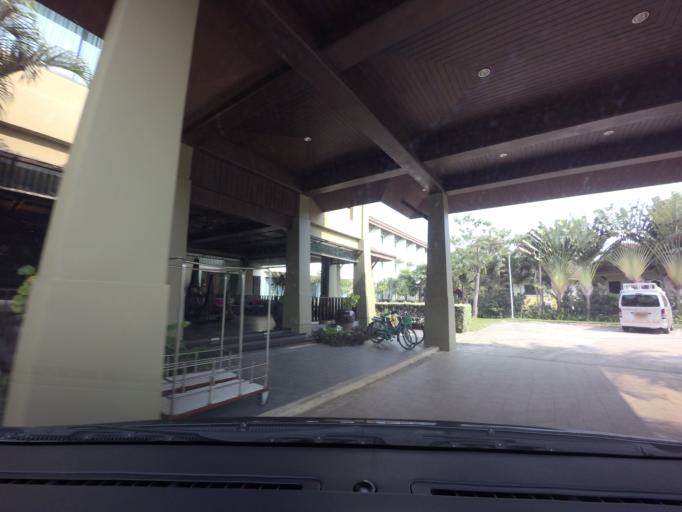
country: TH
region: Prachuap Khiri Khan
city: Kui Buri
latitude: 12.0230
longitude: 99.8883
